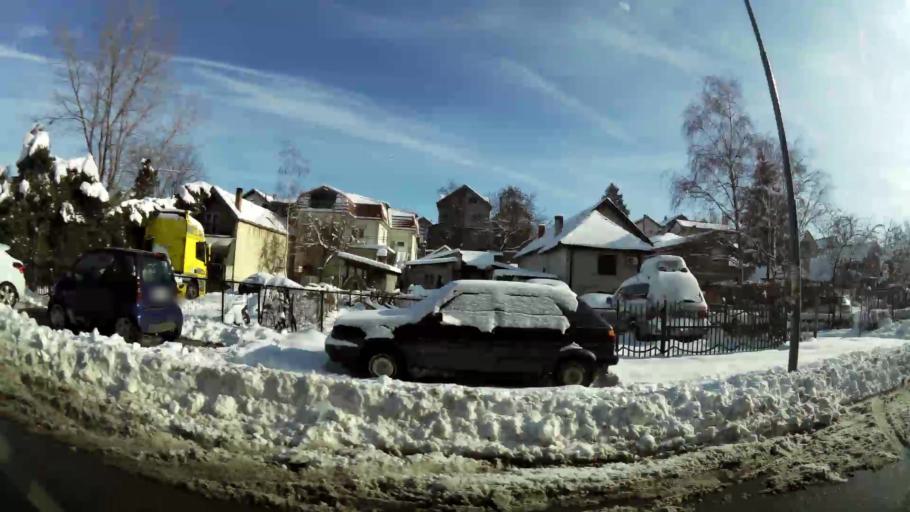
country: RS
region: Central Serbia
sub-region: Belgrade
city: Palilula
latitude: 44.8093
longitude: 20.5242
